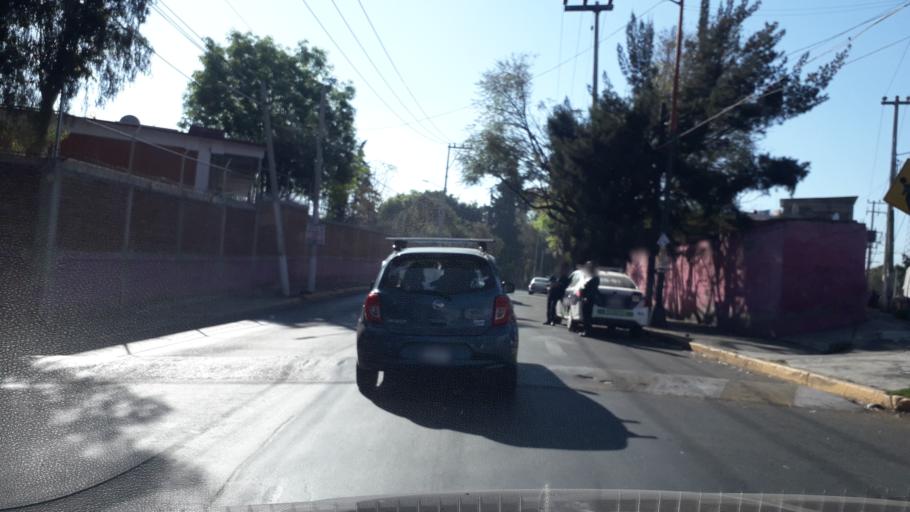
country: MX
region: Mexico City
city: Gustavo A. Madero
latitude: 19.5166
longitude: -99.0891
